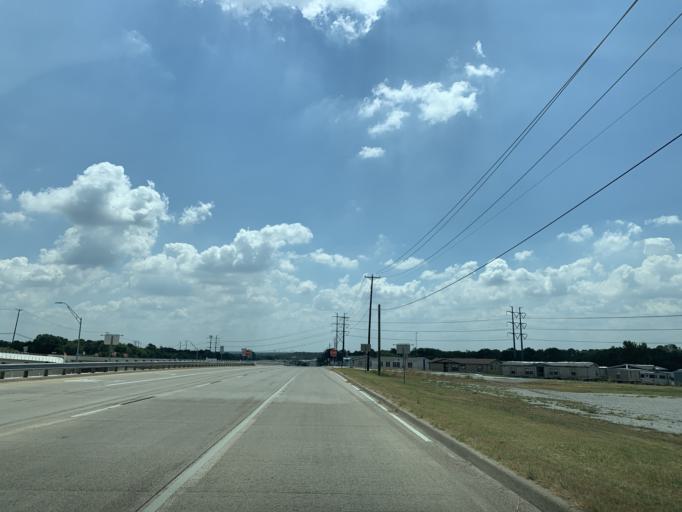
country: US
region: Texas
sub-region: Tarrant County
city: Azle
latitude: 32.8599
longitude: -97.5200
